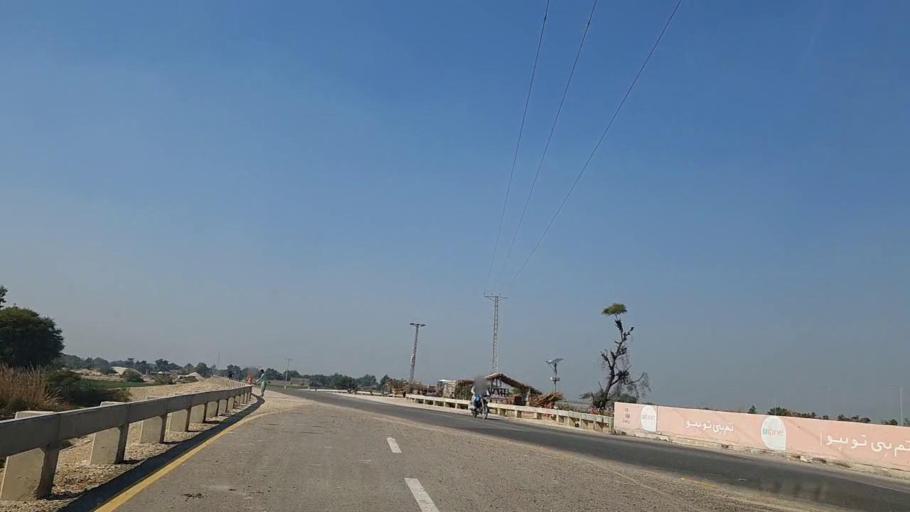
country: PK
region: Sindh
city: Sakrand
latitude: 26.2446
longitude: 68.2623
